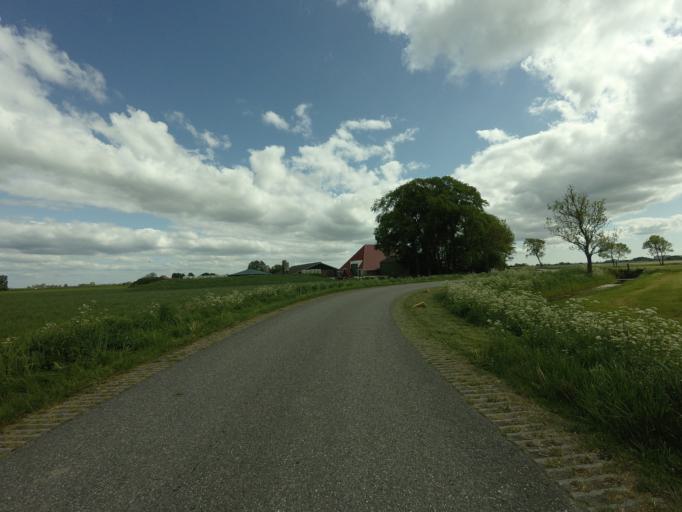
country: NL
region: Friesland
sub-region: Sudwest Fryslan
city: Bolsward
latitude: 53.0796
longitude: 5.5513
